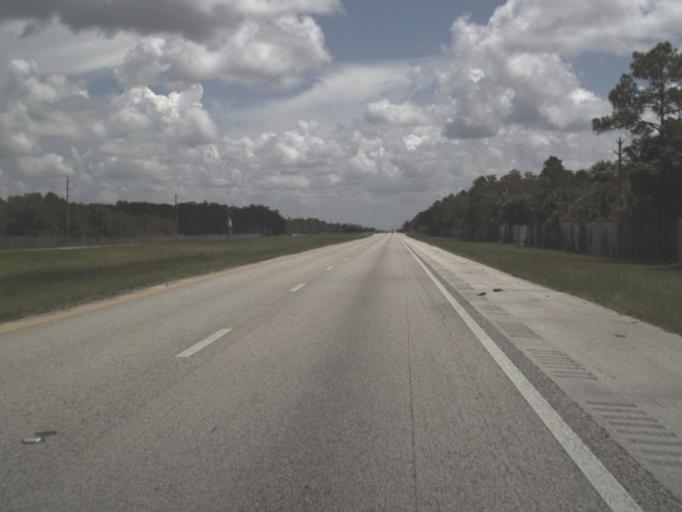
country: US
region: Florida
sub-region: Collier County
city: Immokalee
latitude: 26.1696
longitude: -81.0131
